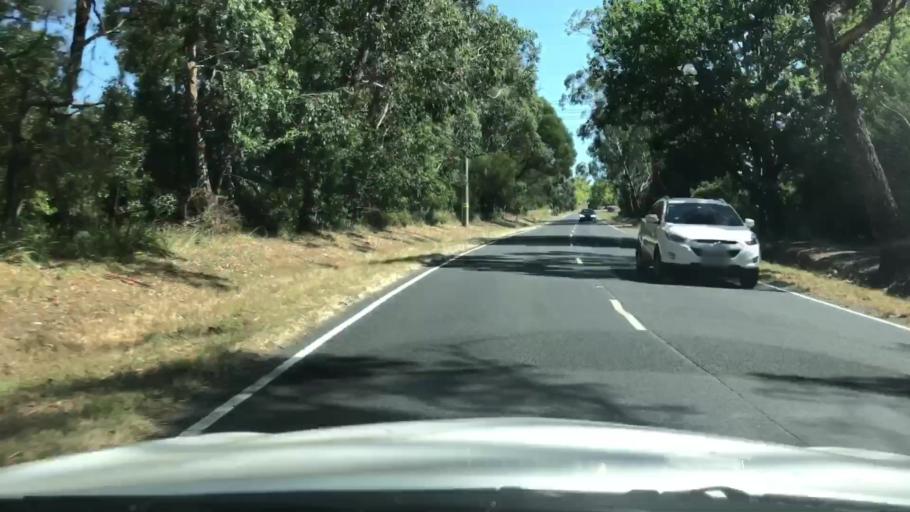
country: AU
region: Victoria
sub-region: Yarra Ranges
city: Woori Yallock
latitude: -37.8040
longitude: 145.5242
